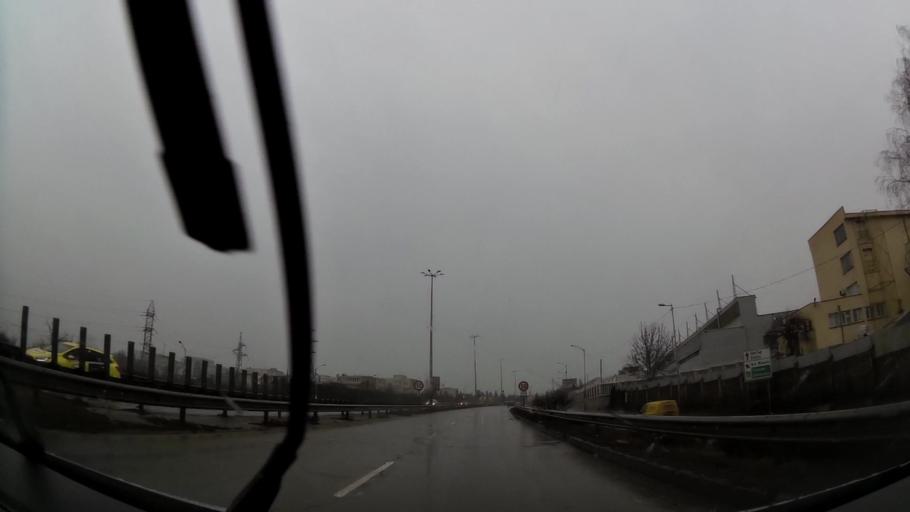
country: BG
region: Sofia-Capital
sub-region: Stolichna Obshtina
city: Sofia
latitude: 42.6599
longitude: 23.3885
